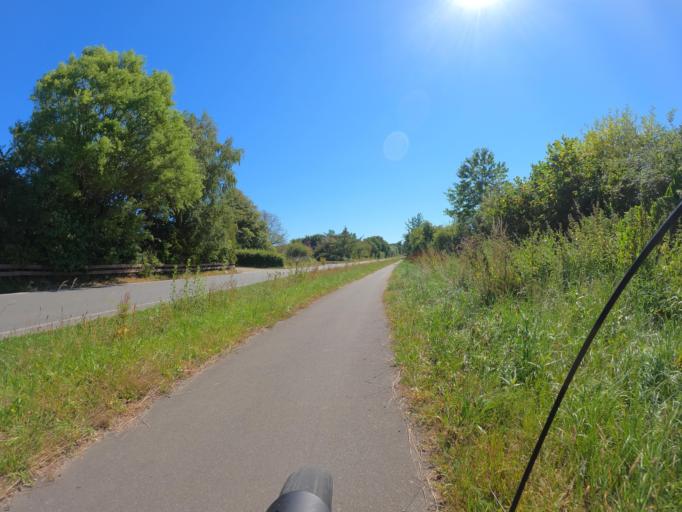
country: DE
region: Schleswig-Holstein
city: Quern
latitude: 54.7879
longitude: 9.7262
